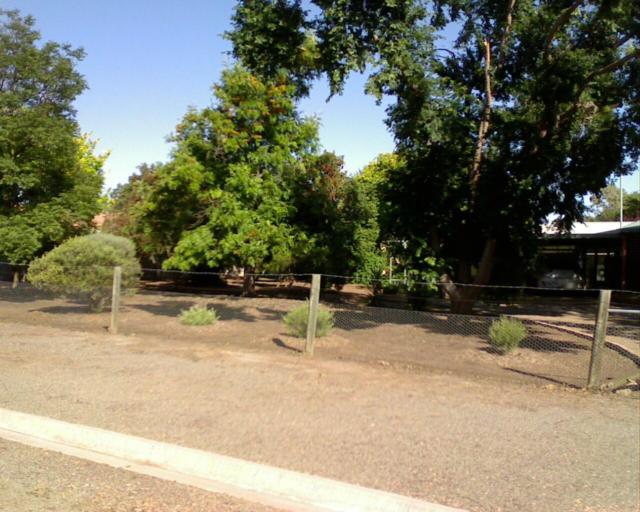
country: AU
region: South Australia
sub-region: Flinders Ranges
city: Quorn
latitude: -32.6521
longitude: 138.1036
